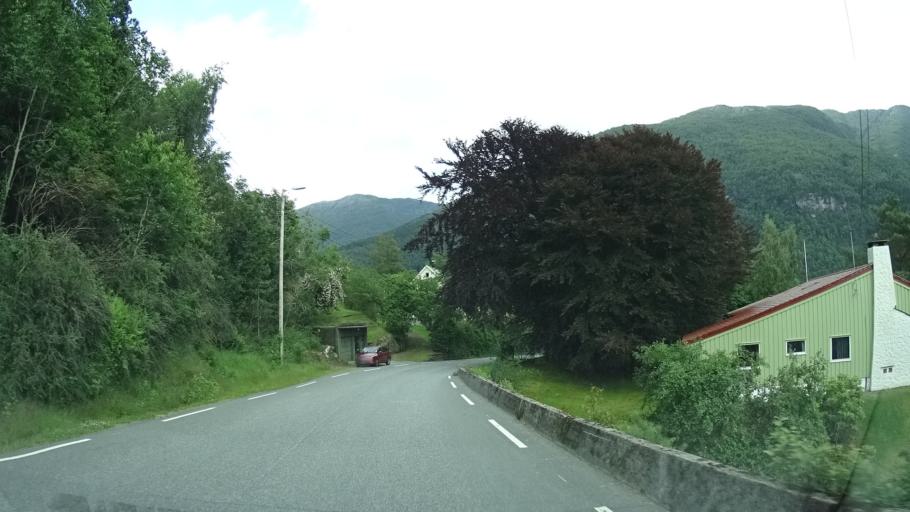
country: NO
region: Hordaland
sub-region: Jondal
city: Jondal
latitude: 60.2818
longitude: 6.2493
